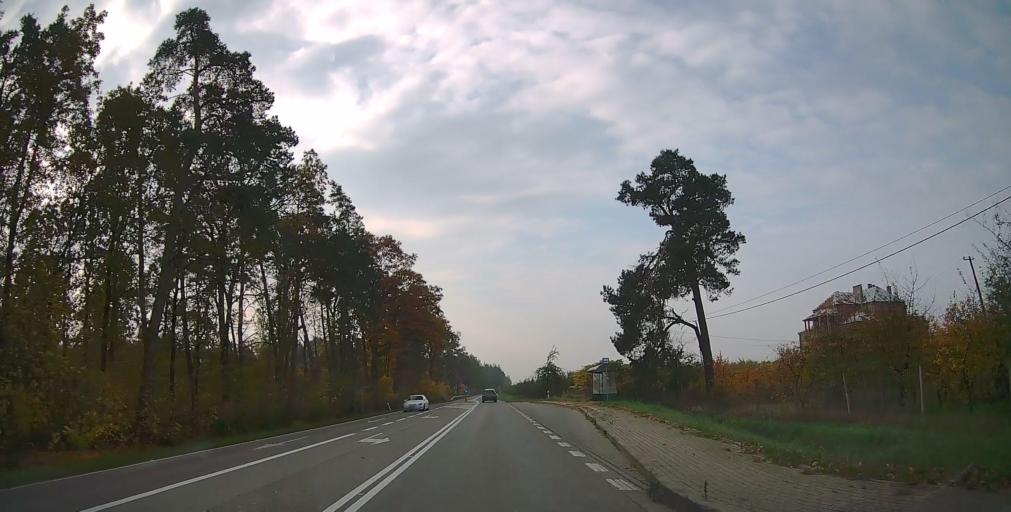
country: PL
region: Masovian Voivodeship
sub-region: Powiat grojecki
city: Belsk Duzy
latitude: 51.7955
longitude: 20.7860
